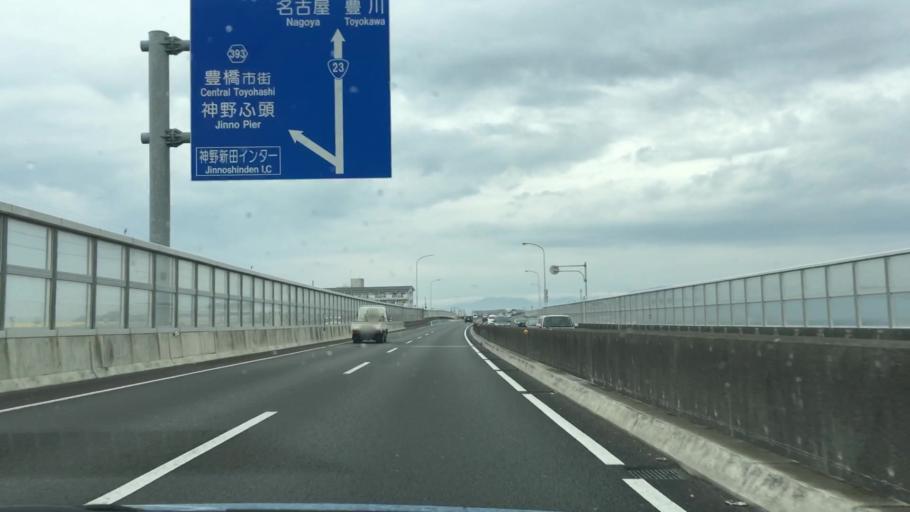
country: JP
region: Aichi
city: Toyohashi
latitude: 34.7357
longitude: 137.3470
